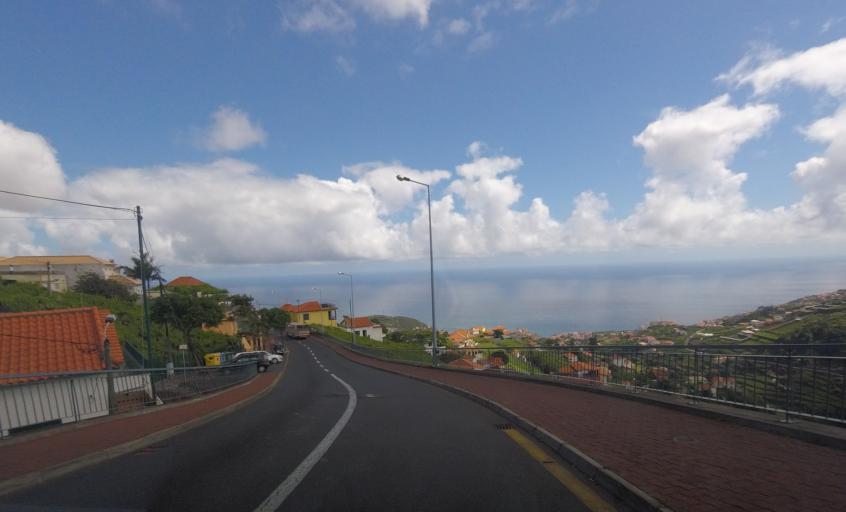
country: PT
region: Madeira
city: Camara de Lobos
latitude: 32.6694
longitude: -16.9800
